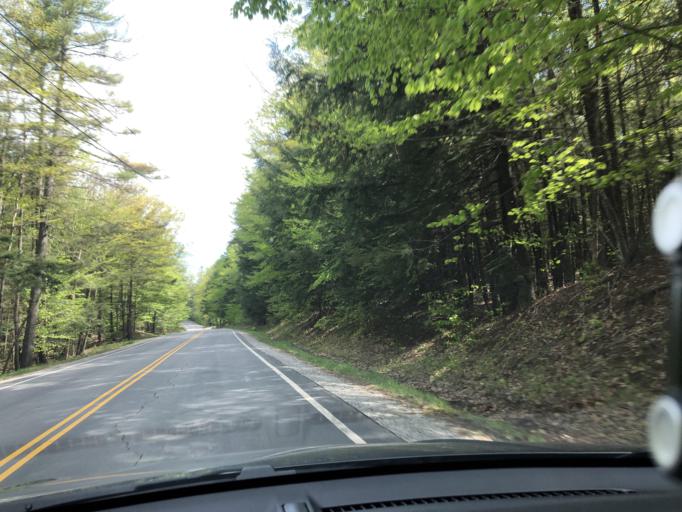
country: US
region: New Hampshire
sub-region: Merrimack County
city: New London
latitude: 43.4176
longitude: -72.0361
